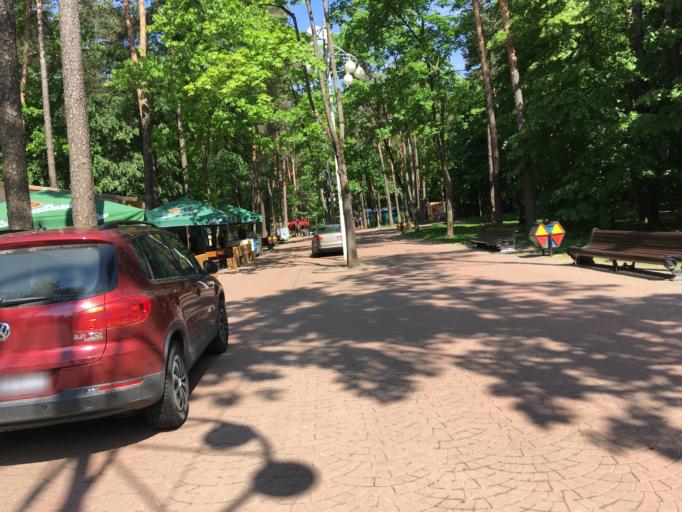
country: BY
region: Minsk
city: Minsk
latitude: 53.9204
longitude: 27.6142
